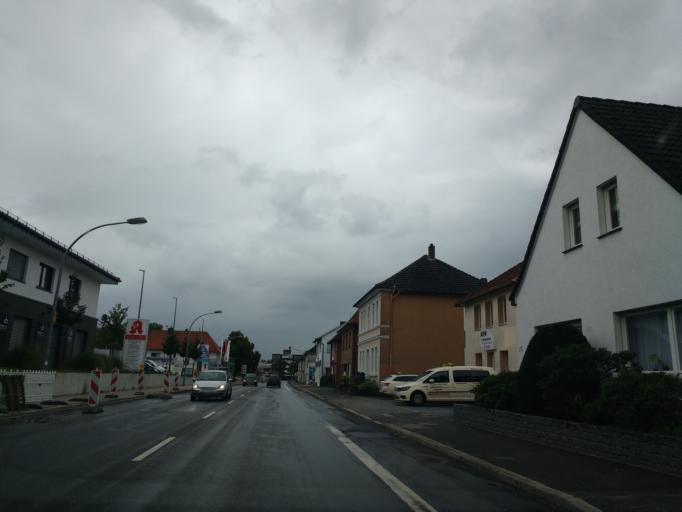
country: DE
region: North Rhine-Westphalia
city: Lengerich
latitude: 52.1923
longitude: 7.8447
